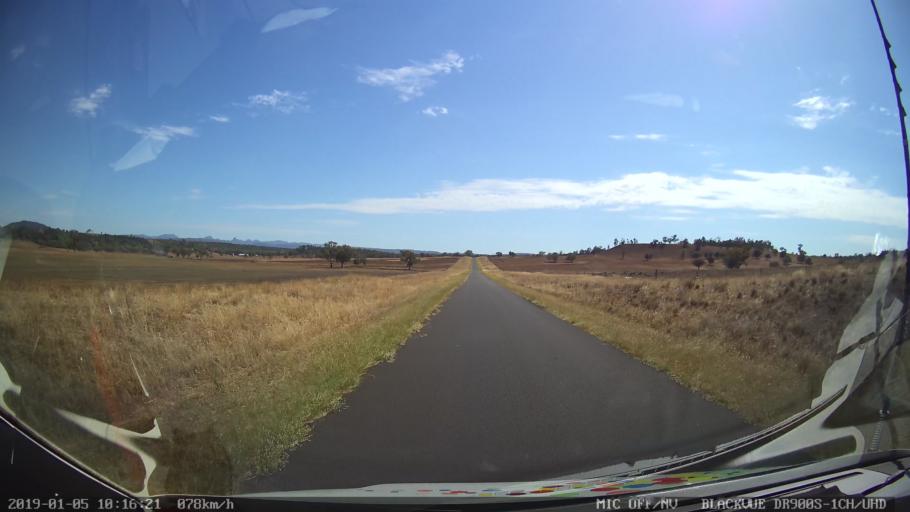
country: AU
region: New South Wales
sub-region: Gilgandra
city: Gilgandra
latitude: -31.5761
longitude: 148.9514
